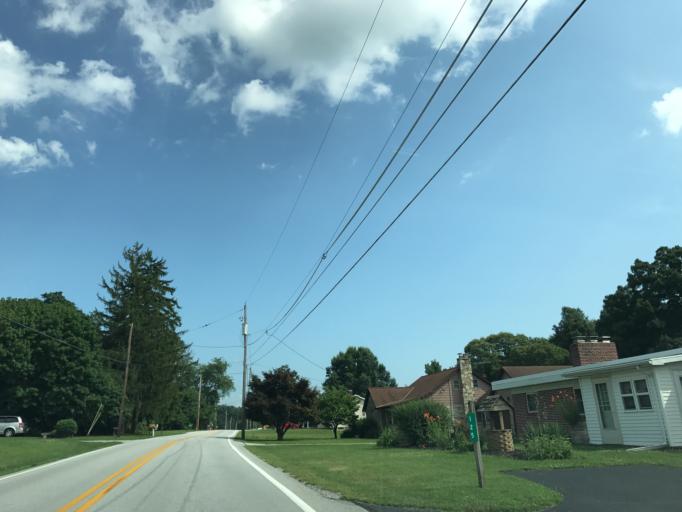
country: US
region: Pennsylvania
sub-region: Adams County
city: Mount Pleasant
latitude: 39.7541
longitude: -77.0337
